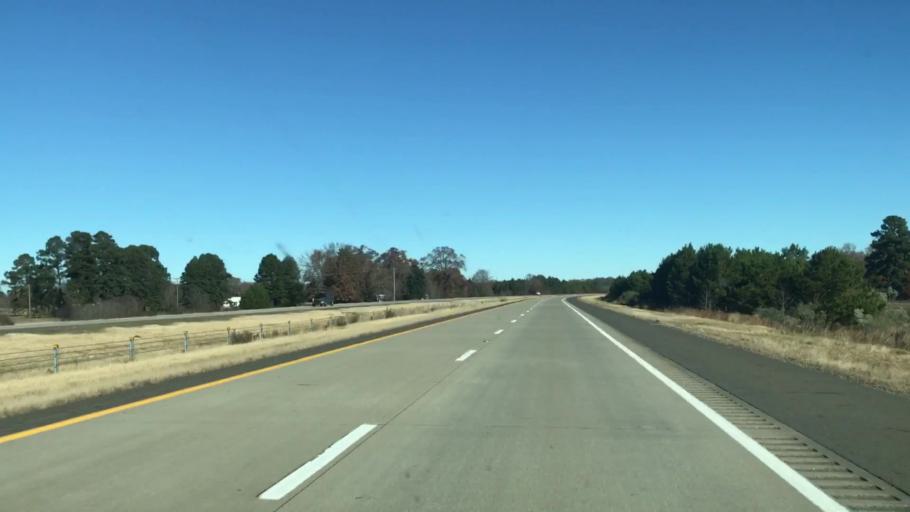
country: US
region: Texas
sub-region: Cass County
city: Queen City
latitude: 33.1964
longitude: -93.8773
